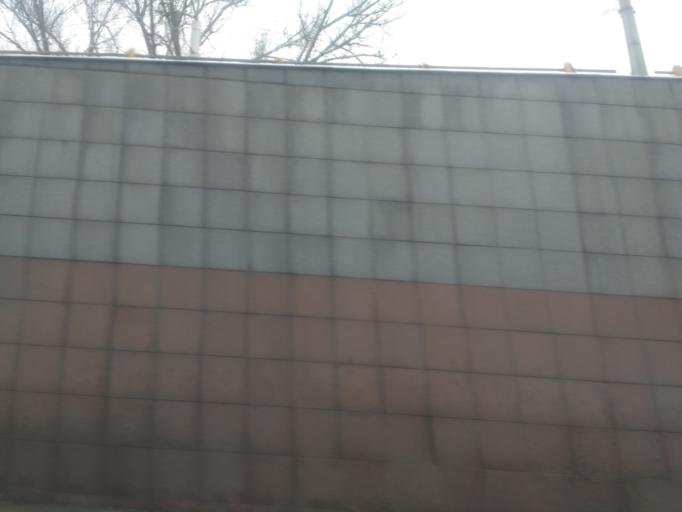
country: KZ
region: Almaty Qalasy
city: Almaty
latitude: 43.2145
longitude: 76.8564
